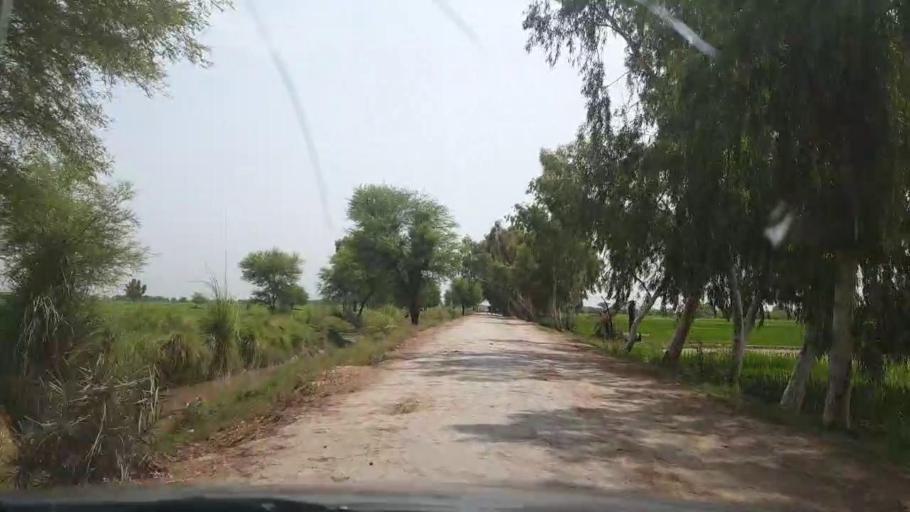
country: PK
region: Sindh
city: Ratodero
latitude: 27.8796
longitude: 68.3341
